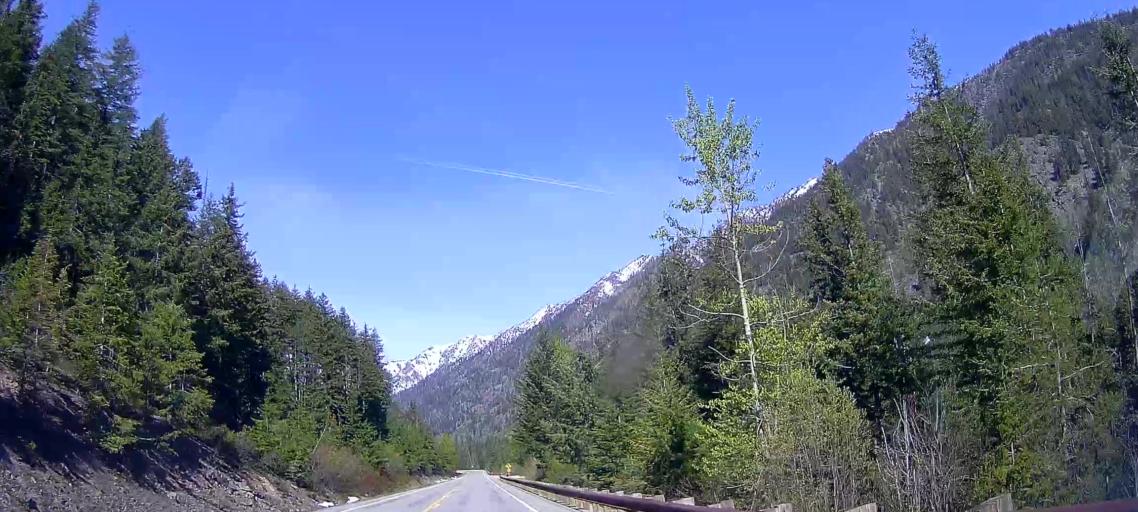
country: US
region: Washington
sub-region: Chelan County
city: Granite Falls
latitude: 48.5981
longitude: -120.5283
